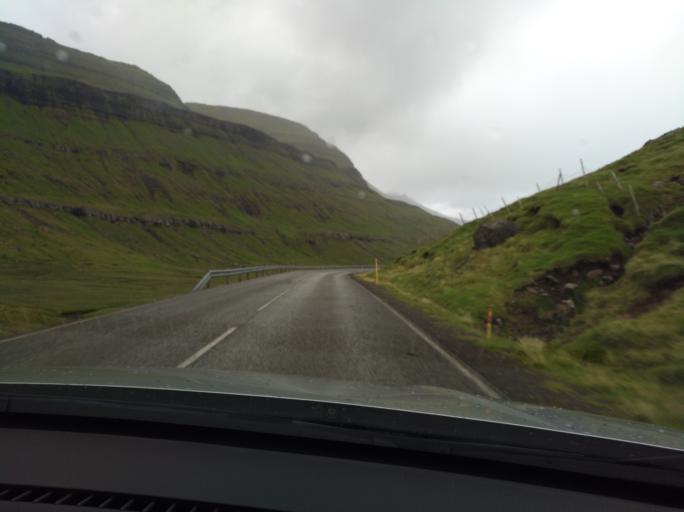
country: FO
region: Eysturoy
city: Fuglafjordur
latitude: 62.2316
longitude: -6.8802
